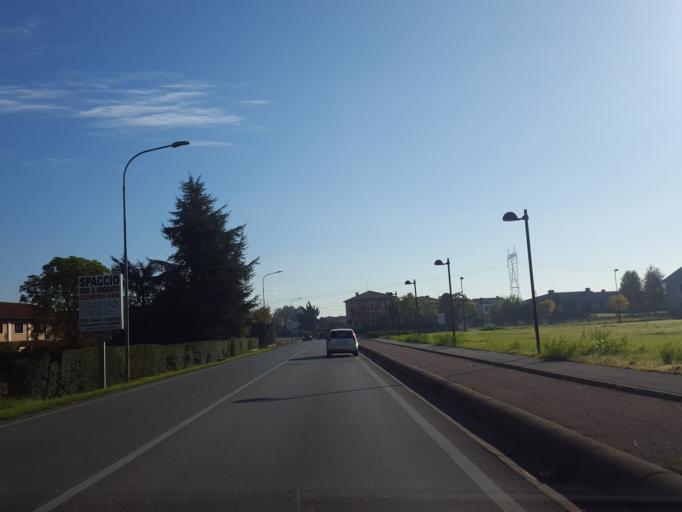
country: IT
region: Veneto
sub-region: Provincia di Vicenza
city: Grumolo delle Abbadesse
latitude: 45.5211
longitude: 11.6625
